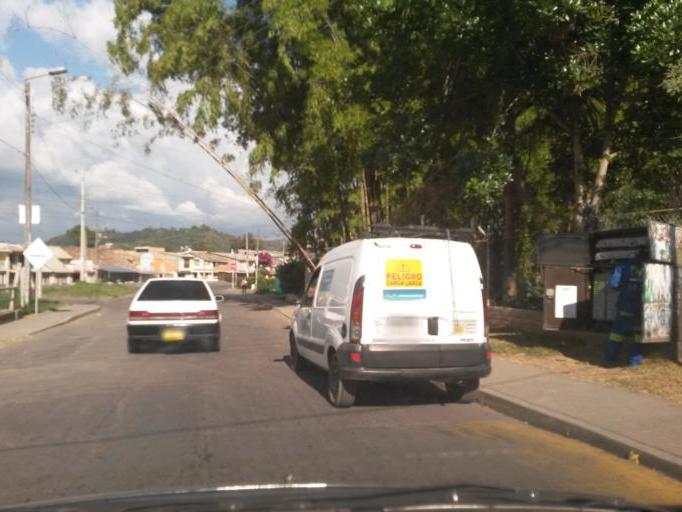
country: CO
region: Cauca
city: Popayan
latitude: 2.4342
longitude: -76.6143
